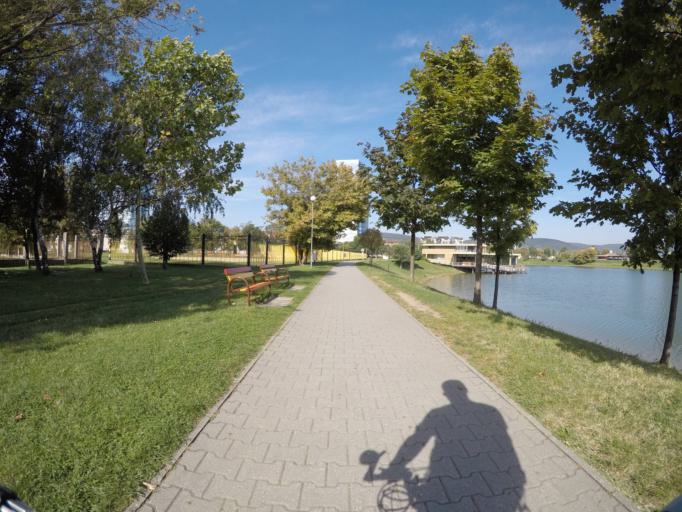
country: SK
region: Bratislavsky
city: Bratislava
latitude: 48.1688
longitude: 17.1436
